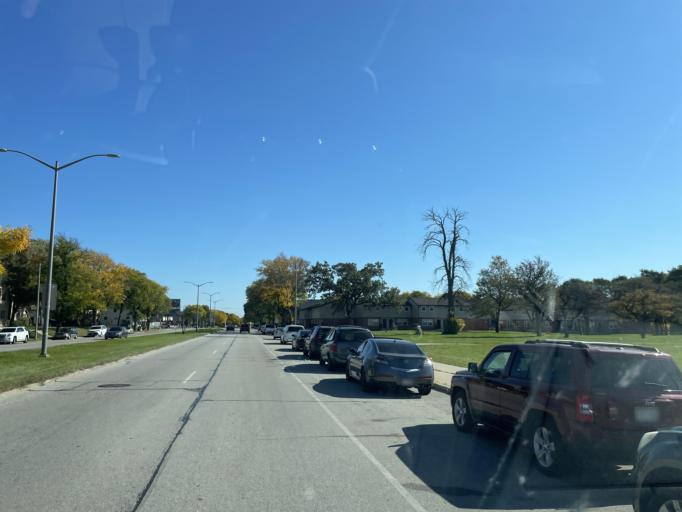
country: US
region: Wisconsin
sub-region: Waukesha County
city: Butler
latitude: 43.1111
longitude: -88.0241
